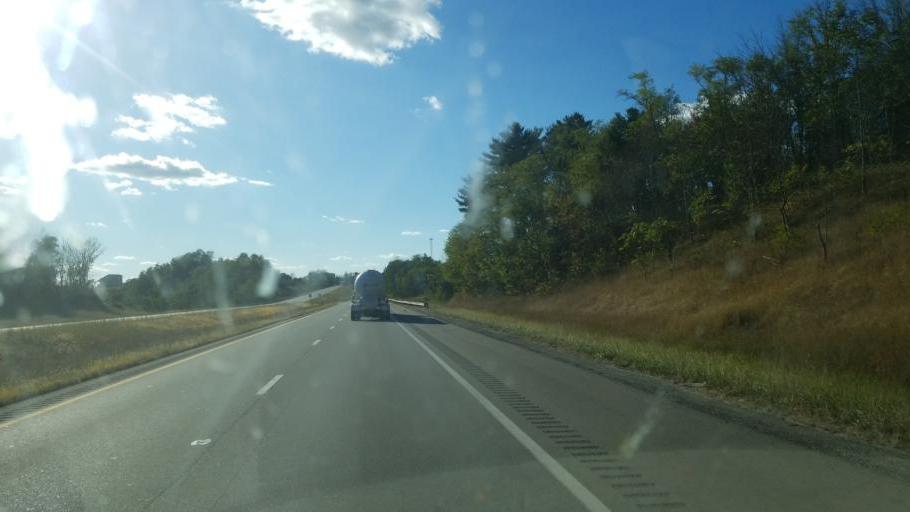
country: US
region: Ohio
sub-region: Belmont County
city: Barnesville
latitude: 40.0557
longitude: -81.2745
